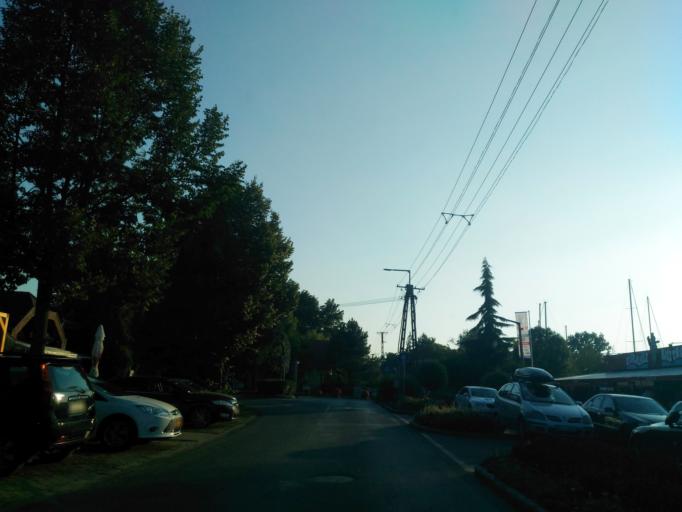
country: HU
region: Somogy
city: Balatonszarszo
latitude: 46.8118
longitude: 17.7720
